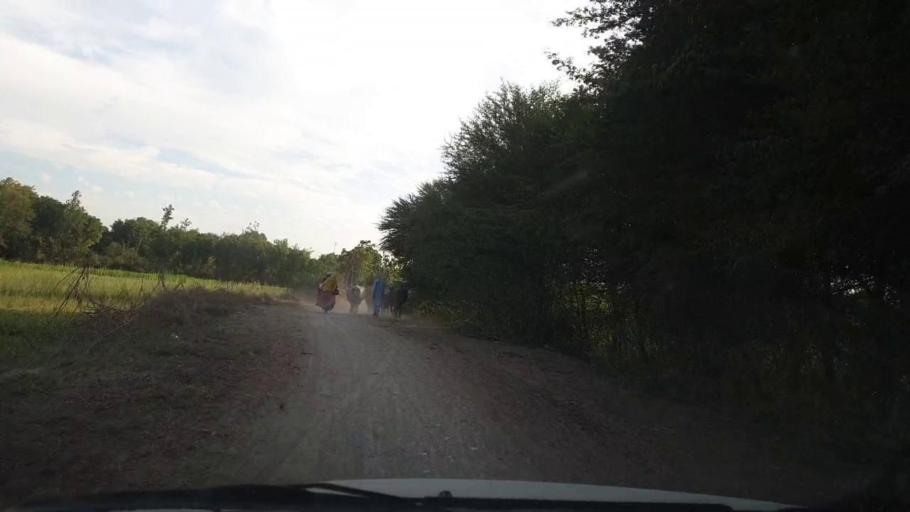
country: PK
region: Sindh
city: Pithoro
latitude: 25.6411
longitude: 69.2917
